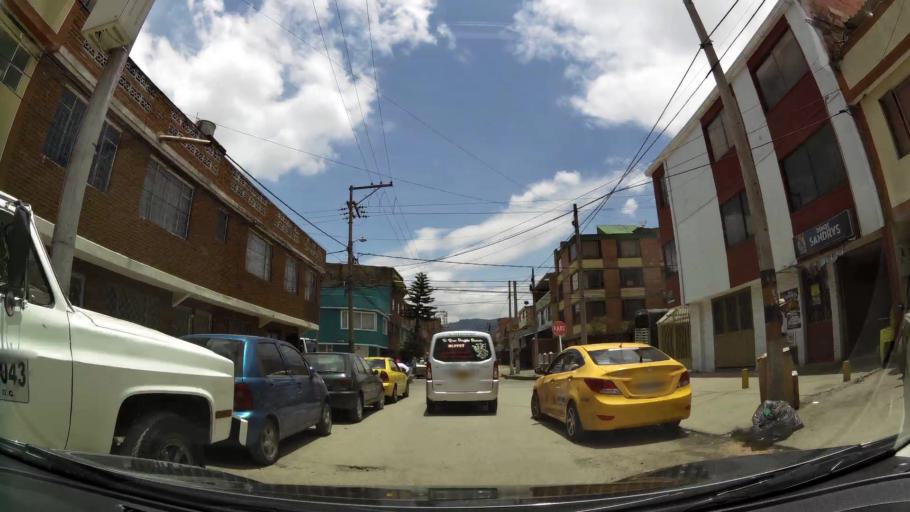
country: CO
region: Bogota D.C.
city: Barrio San Luis
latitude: 4.7131
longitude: -74.0617
